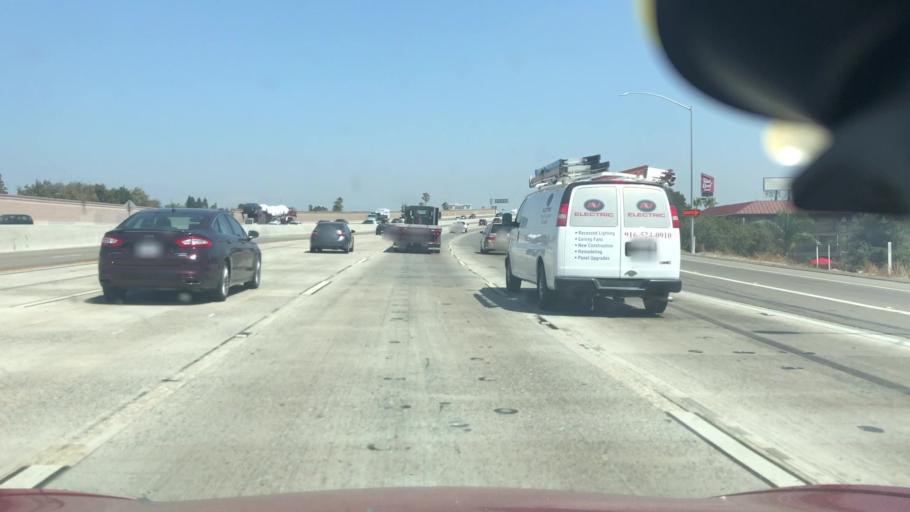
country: US
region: California
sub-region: San Joaquin County
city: Country Club
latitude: 37.9554
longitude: -121.3176
